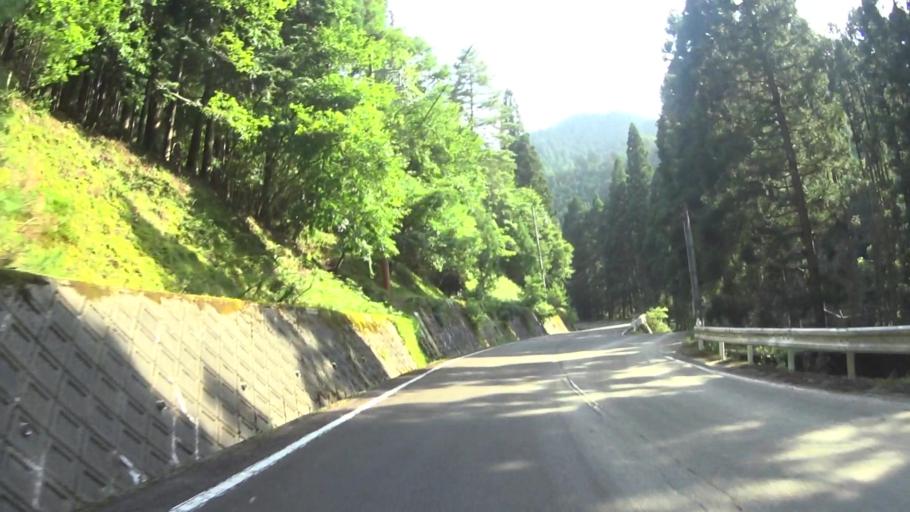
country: JP
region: Fukui
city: Obama
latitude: 35.2749
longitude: 135.6893
